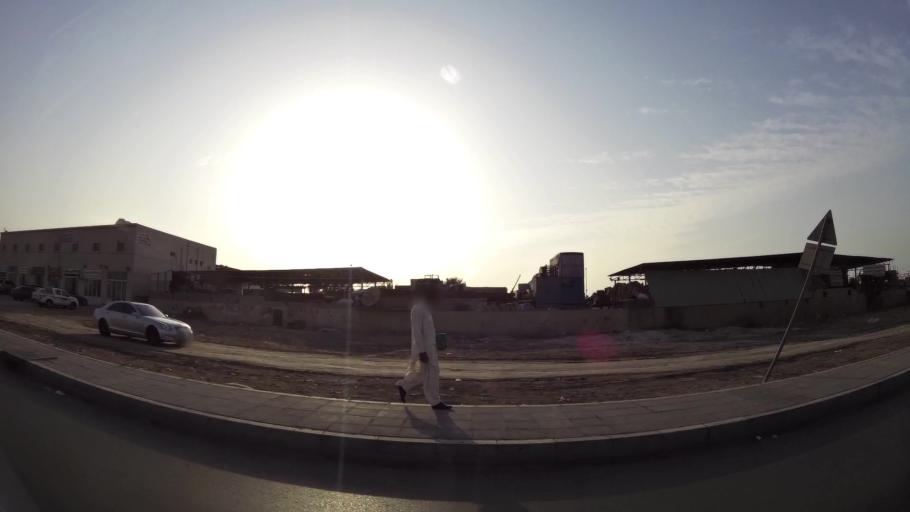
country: AE
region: Abu Dhabi
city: Abu Dhabi
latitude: 24.3581
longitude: 54.5116
